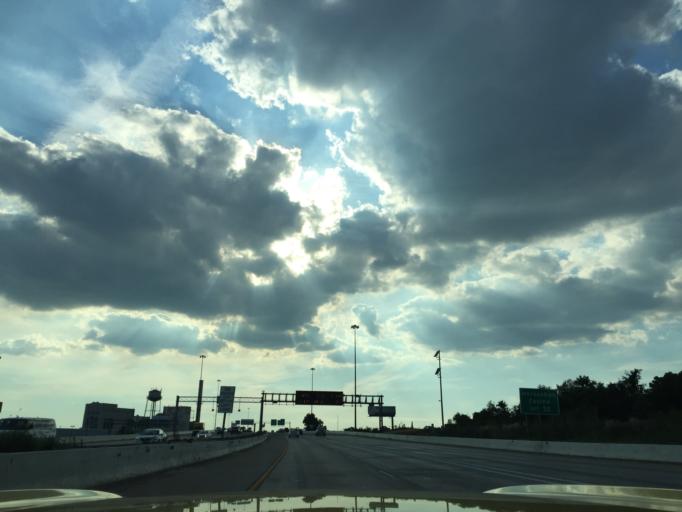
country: US
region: Maryland
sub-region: City of Baltimore
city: Baltimore
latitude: 39.2661
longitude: -76.5960
